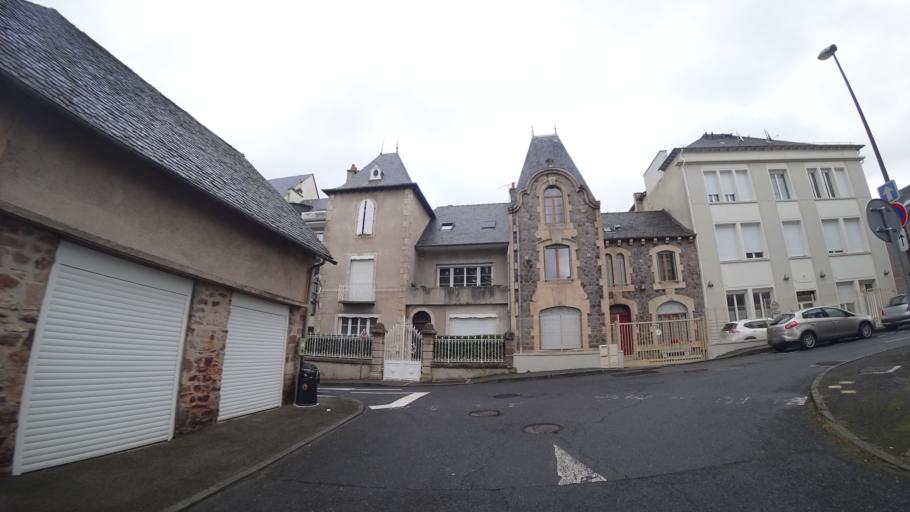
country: FR
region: Midi-Pyrenees
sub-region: Departement de l'Aveyron
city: Rodez
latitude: 44.3540
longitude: 2.5708
